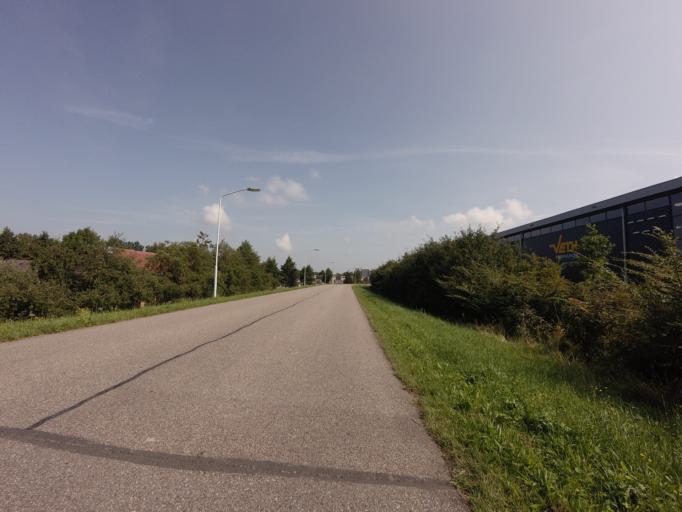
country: NL
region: South Holland
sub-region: Gemeente Papendrecht
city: Papendrecht
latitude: 51.8297
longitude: 4.7134
